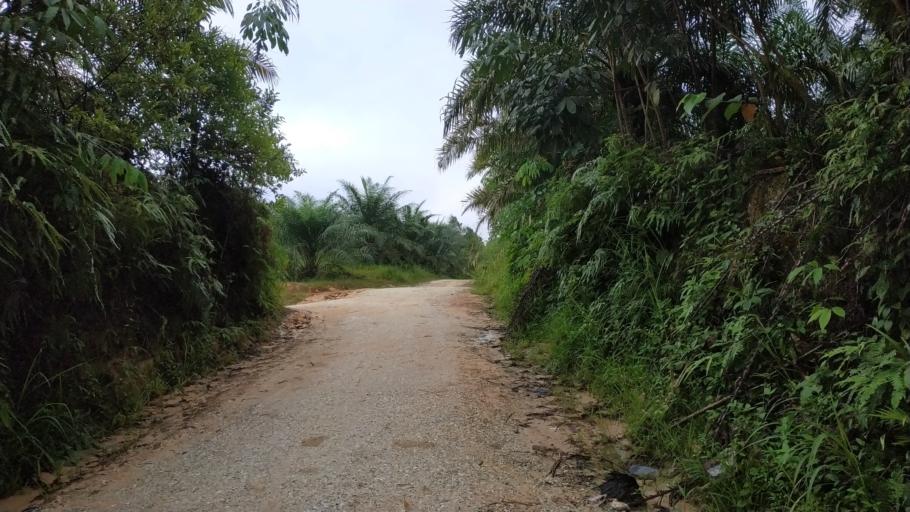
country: ID
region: Riau
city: Pekanbaru
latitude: 0.4817
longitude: 101.5627
